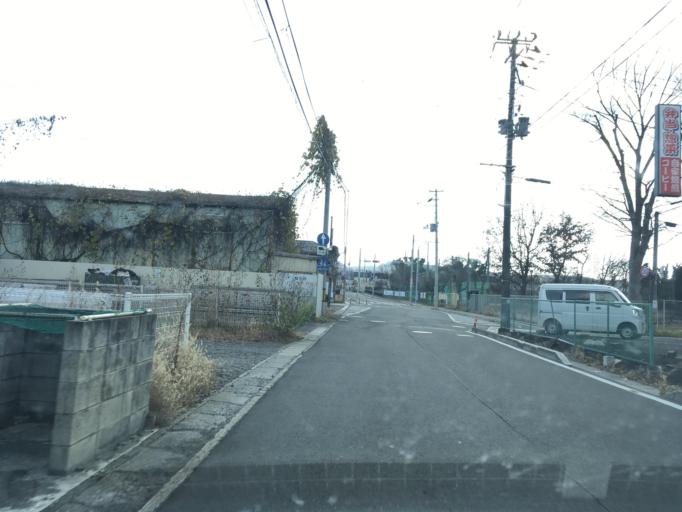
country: JP
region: Miyagi
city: Sendai
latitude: 38.2745
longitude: 140.7644
